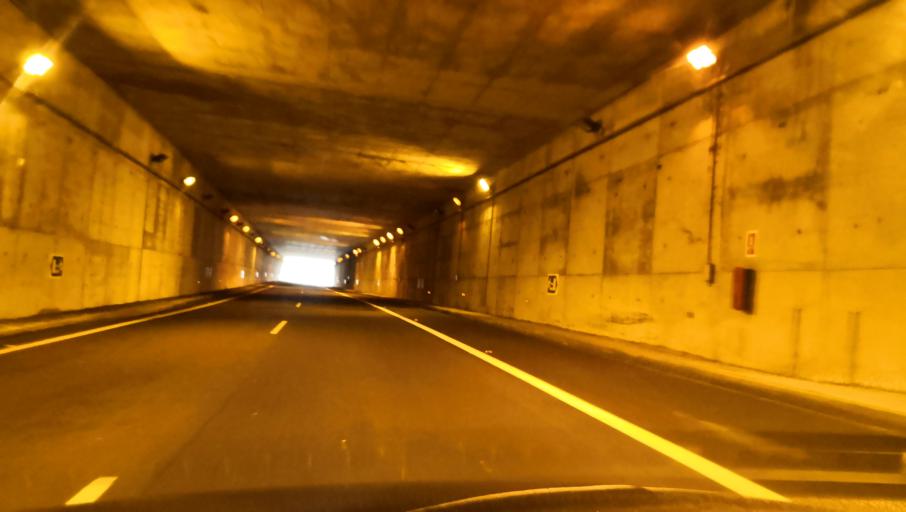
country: ES
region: Galicia
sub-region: Provincia da Coruna
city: Ribeira
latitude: 42.7526
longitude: -8.3937
